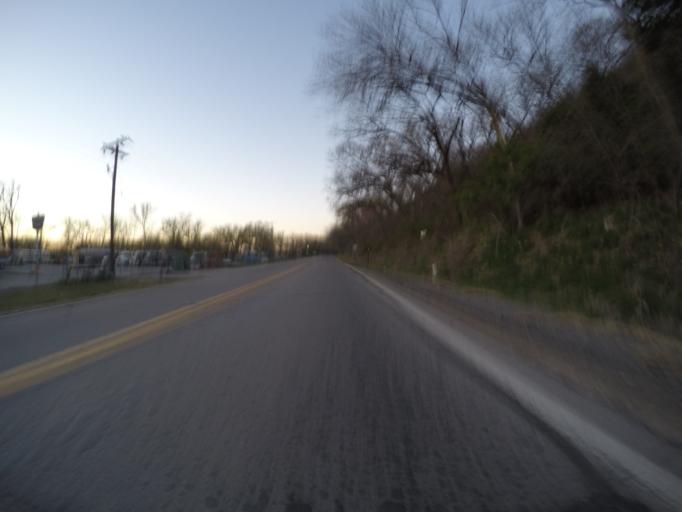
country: US
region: Kansas
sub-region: Riley County
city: Manhattan
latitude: 39.1682
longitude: -96.5535
